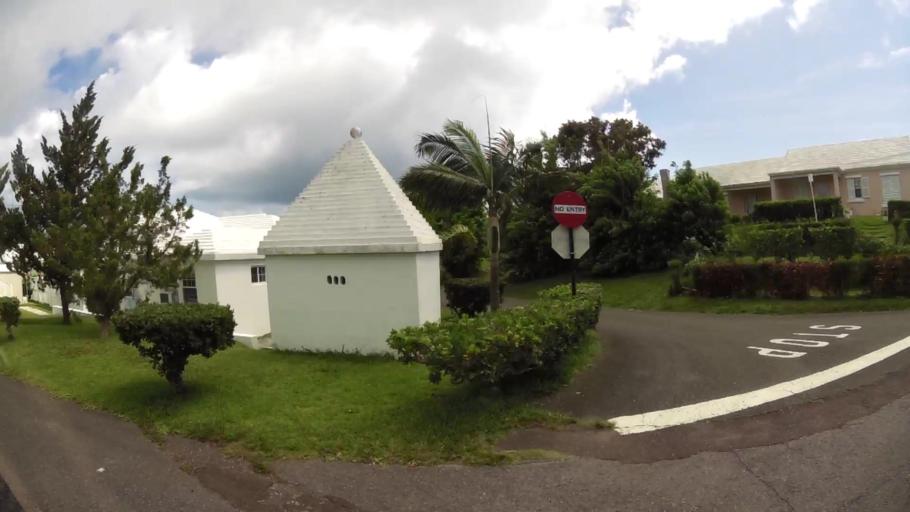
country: BM
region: Saint George
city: Saint George
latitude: 32.3673
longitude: -64.6731
